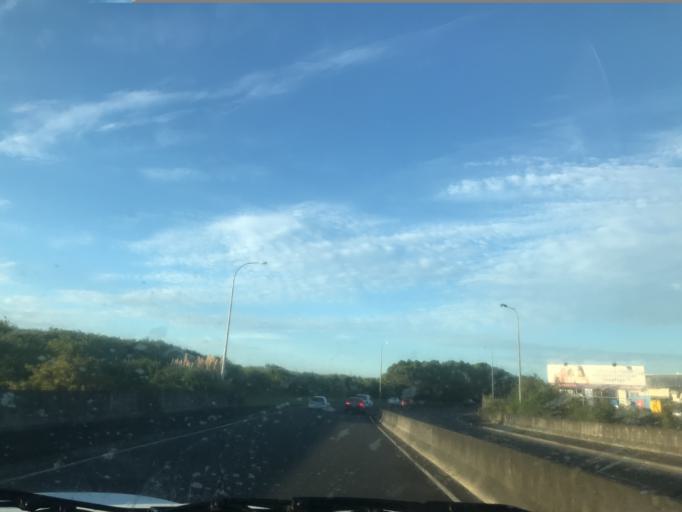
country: NZ
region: Auckland
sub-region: Auckland
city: Tamaki
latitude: -36.9124
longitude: 174.8525
